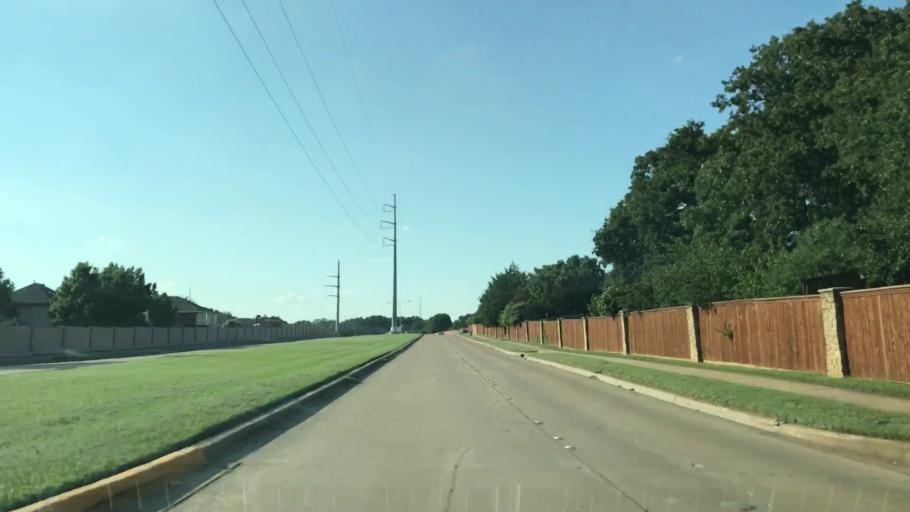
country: US
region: Texas
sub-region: Denton County
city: Lewisville
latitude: 33.0303
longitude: -97.0320
